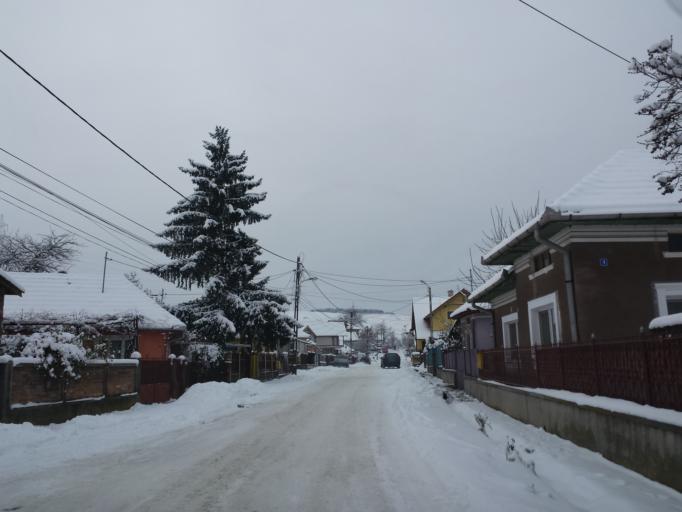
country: RO
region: Hunedoara
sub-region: Municipiul Deva
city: Cristur
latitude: 45.8229
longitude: 22.9266
